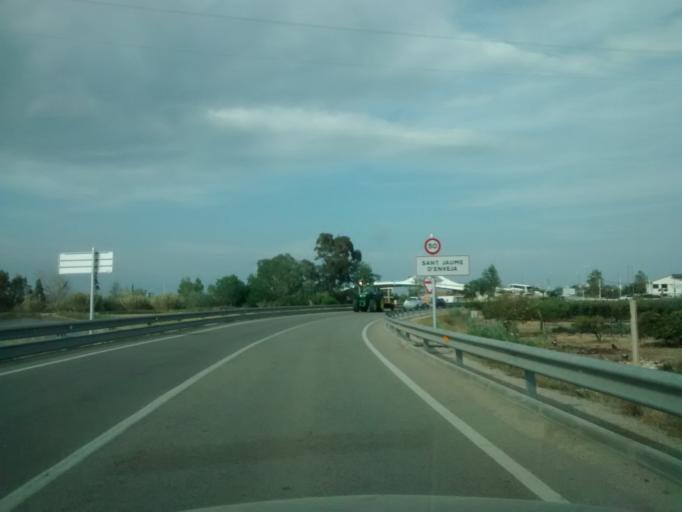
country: ES
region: Catalonia
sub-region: Provincia de Tarragona
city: Deltebre
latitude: 40.7103
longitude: 0.7147
